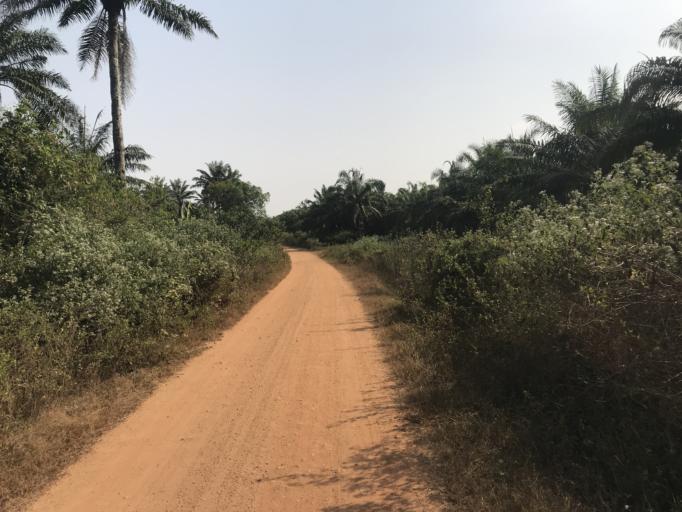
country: NG
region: Osun
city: Olupona
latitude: 7.6133
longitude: 4.1502
